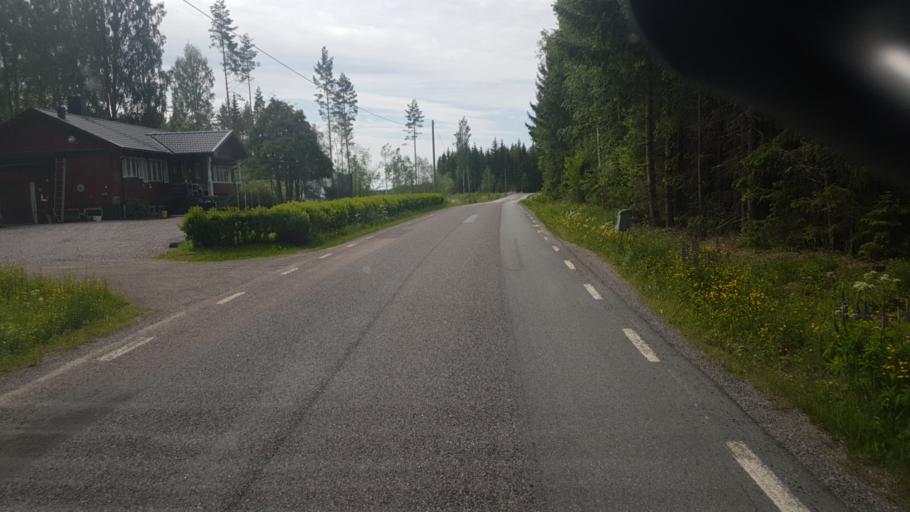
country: SE
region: Vaermland
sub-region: Eda Kommun
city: Charlottenberg
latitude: 59.8803
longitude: 12.3539
